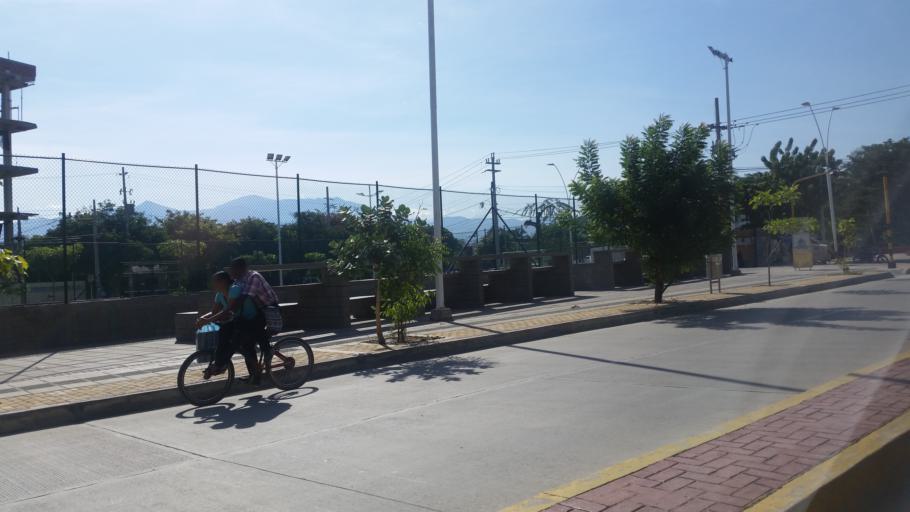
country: CO
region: Magdalena
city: Santa Marta
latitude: 11.2341
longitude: -74.2100
